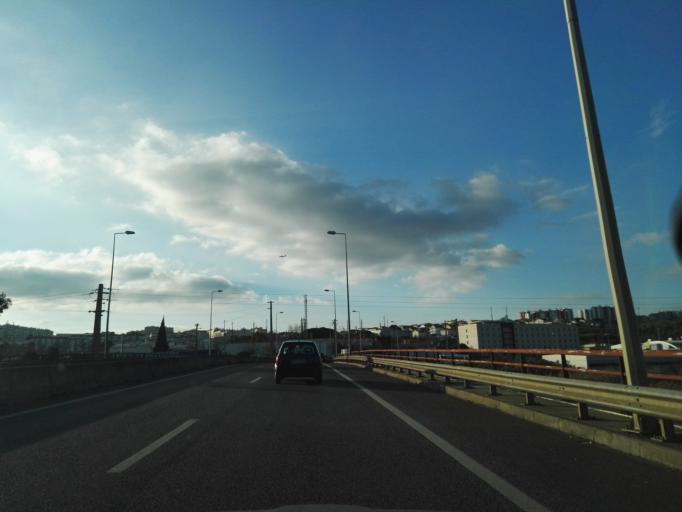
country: PT
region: Lisbon
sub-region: Loures
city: Santa Iria da Azoia
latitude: 38.8367
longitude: -9.0806
